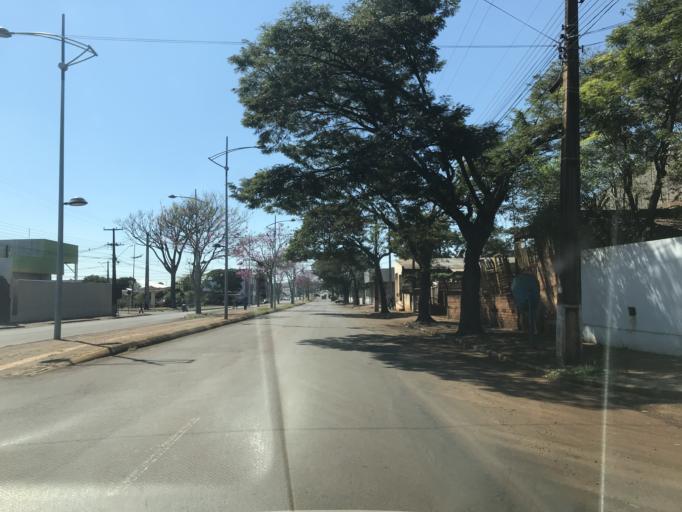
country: BR
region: Parana
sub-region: Toledo
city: Toledo
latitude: -24.7222
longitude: -53.7190
